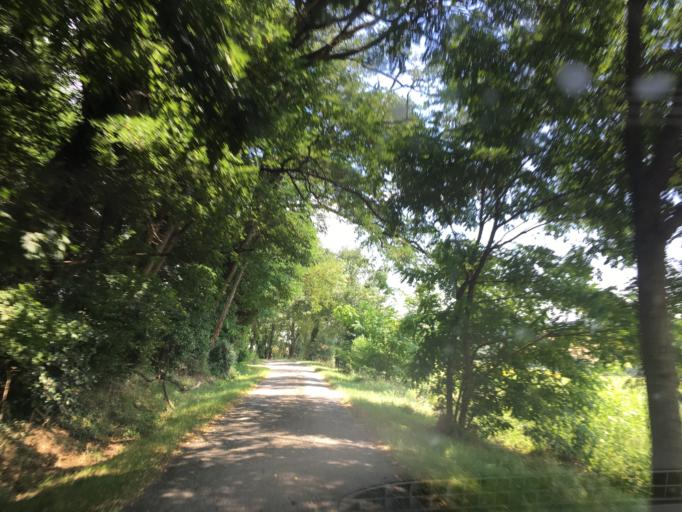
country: FR
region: Midi-Pyrenees
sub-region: Departement du Gers
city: Jegun
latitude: 43.7894
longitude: 0.4814
